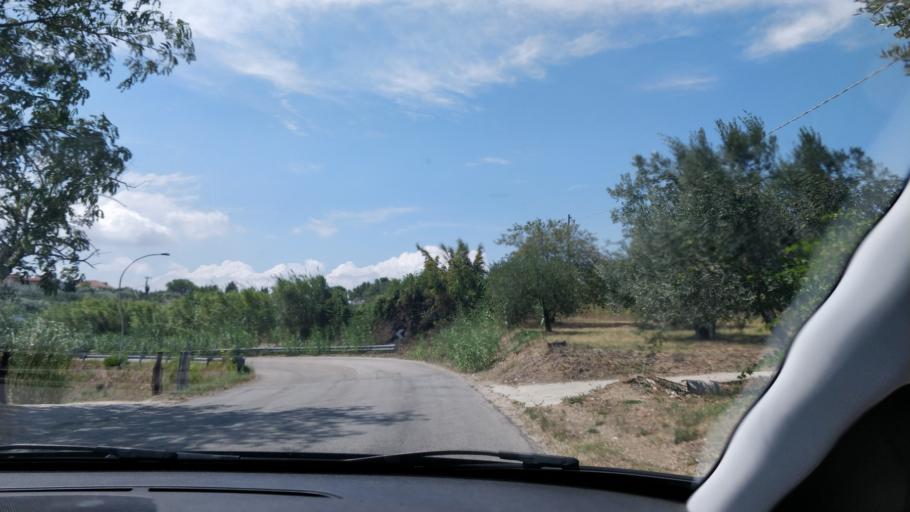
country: IT
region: Abruzzo
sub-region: Provincia di Chieti
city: Francavilla al Mare
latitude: 42.4221
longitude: 14.2497
